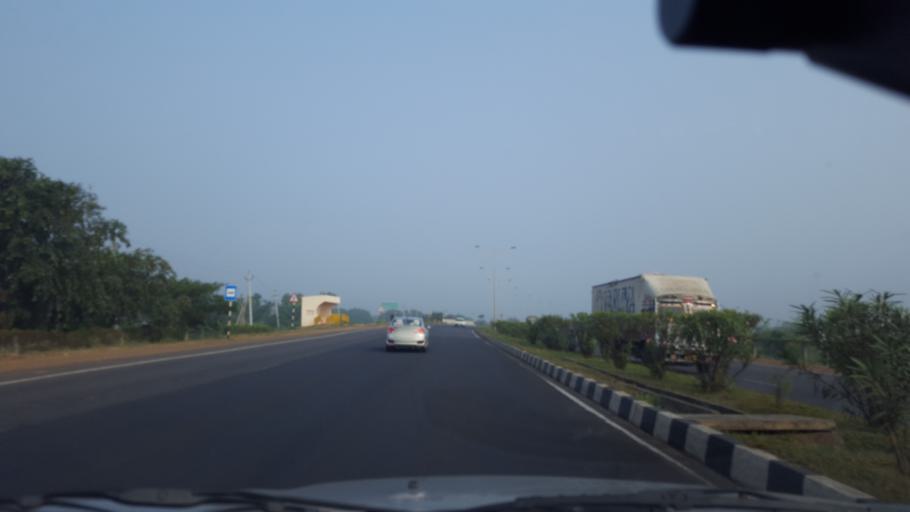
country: IN
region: Andhra Pradesh
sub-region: Prakasam
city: Ongole
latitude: 15.3857
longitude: 80.0398
